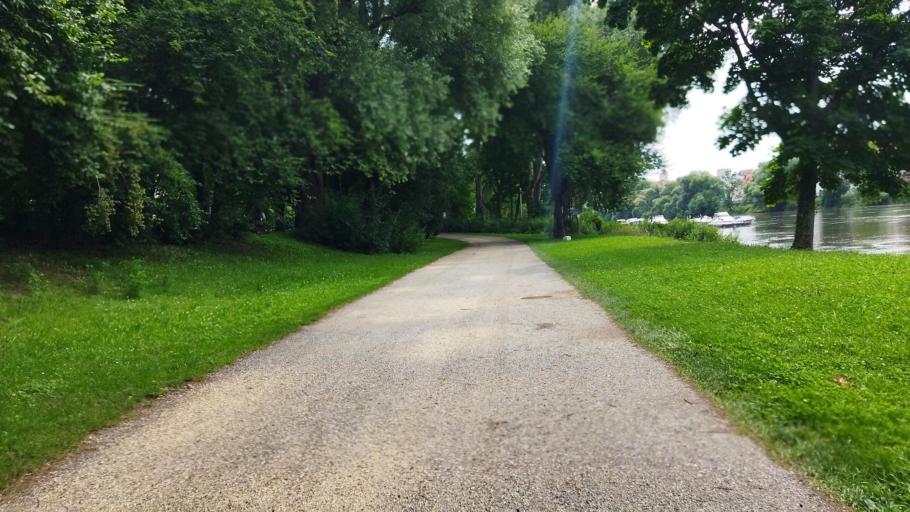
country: DE
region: Bavaria
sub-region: Upper Palatinate
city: Lappersdorf
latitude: 49.0239
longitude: 12.0849
